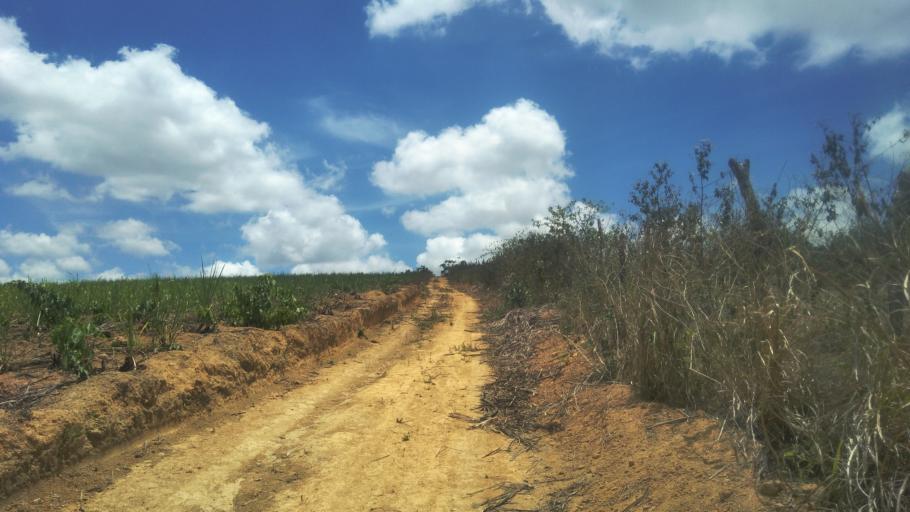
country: BR
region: Pernambuco
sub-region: Vitoria De Santo Antao
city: Vitoria de Santo Antao
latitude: -8.1517
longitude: -35.2540
